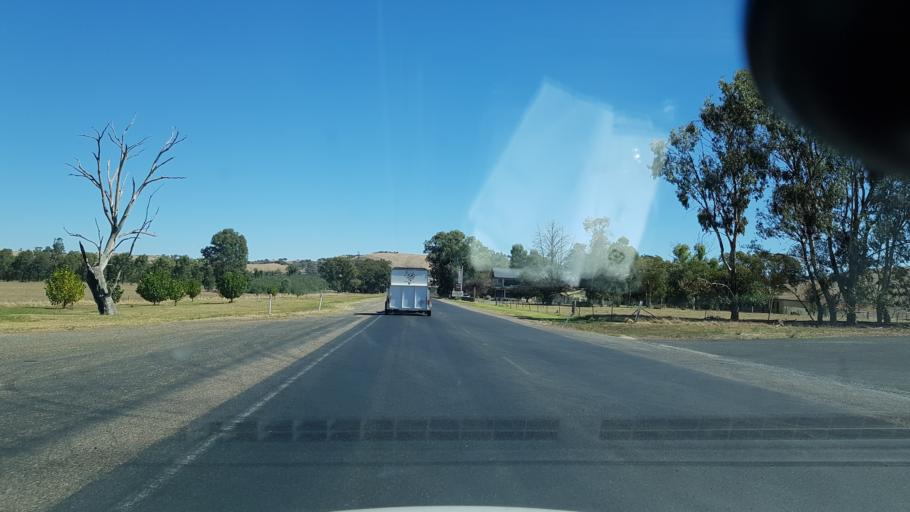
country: AU
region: New South Wales
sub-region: Gundagai
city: Gundagai
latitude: -34.8225
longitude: 148.3425
